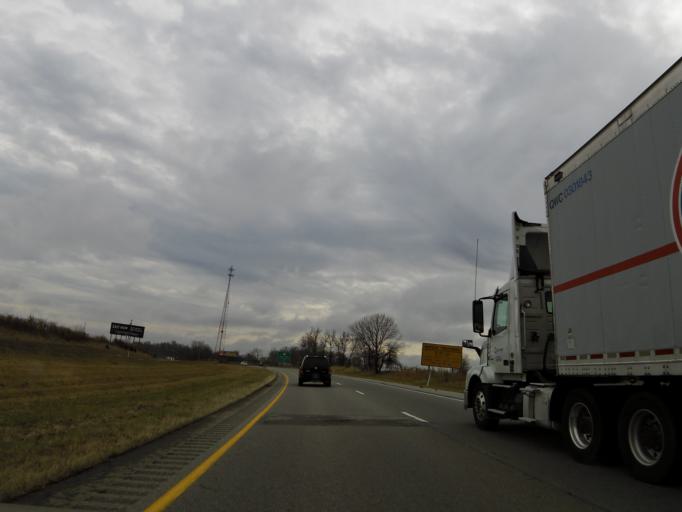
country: US
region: Indiana
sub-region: Dearborn County
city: Bright
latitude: 39.2800
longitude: -84.9686
